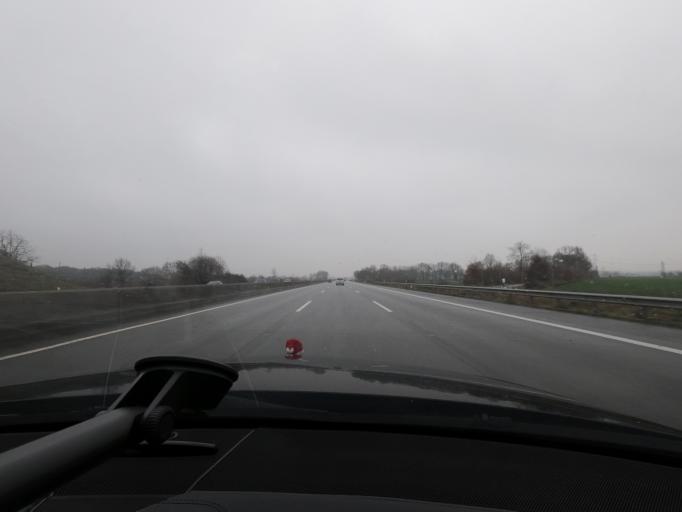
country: DE
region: Schleswig-Holstein
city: Grossenaspe
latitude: 53.9825
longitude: 9.9435
